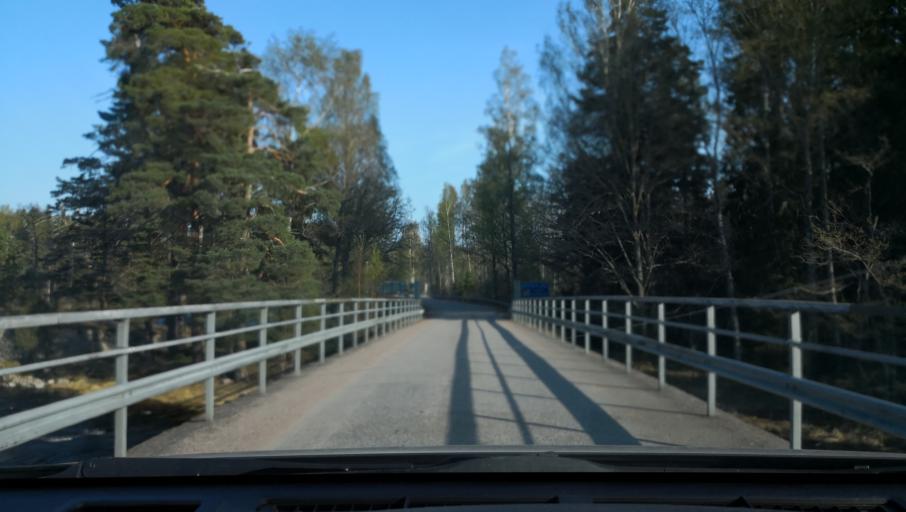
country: SE
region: Uppsala
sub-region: Heby Kommun
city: Tarnsjo
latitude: 60.2694
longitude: 16.9098
